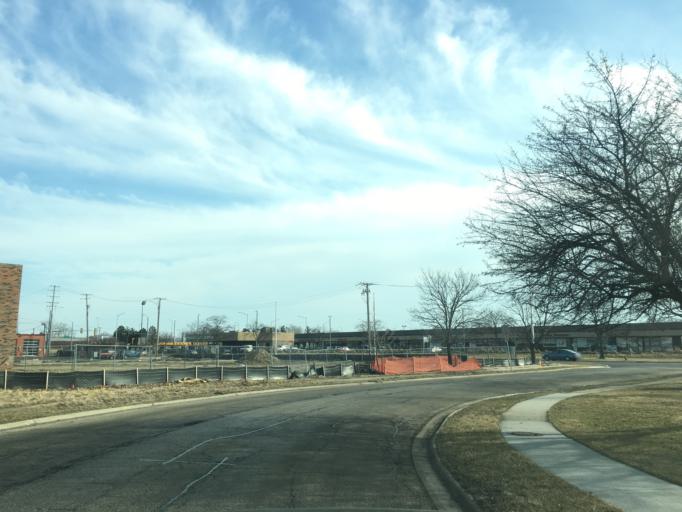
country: US
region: Illinois
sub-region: Cook County
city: Hoffman Estates
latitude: 42.0468
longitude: -88.1003
